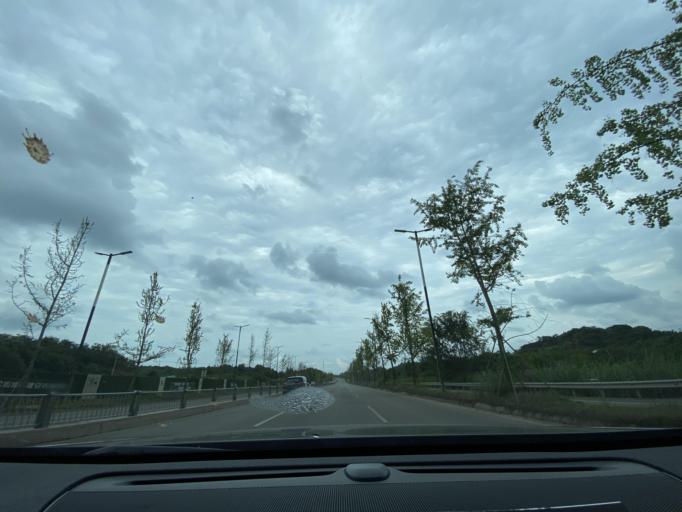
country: CN
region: Sichuan
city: Jiancheng
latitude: 30.4915
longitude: 104.4690
